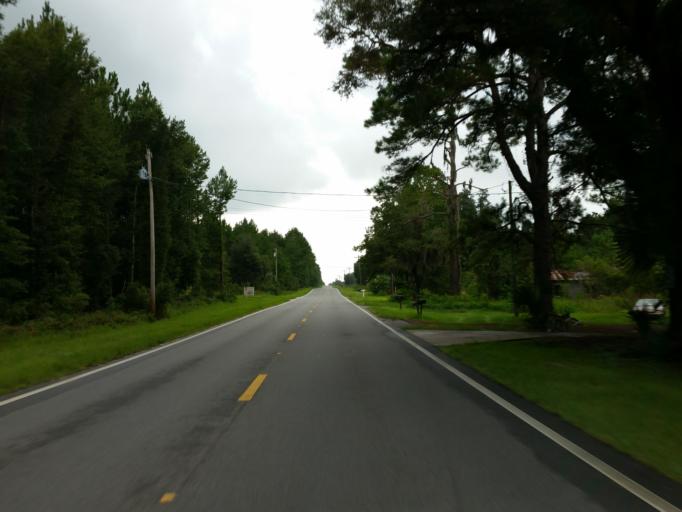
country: US
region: Florida
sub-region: Levy County
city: Williston
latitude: 29.4072
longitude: -82.3044
